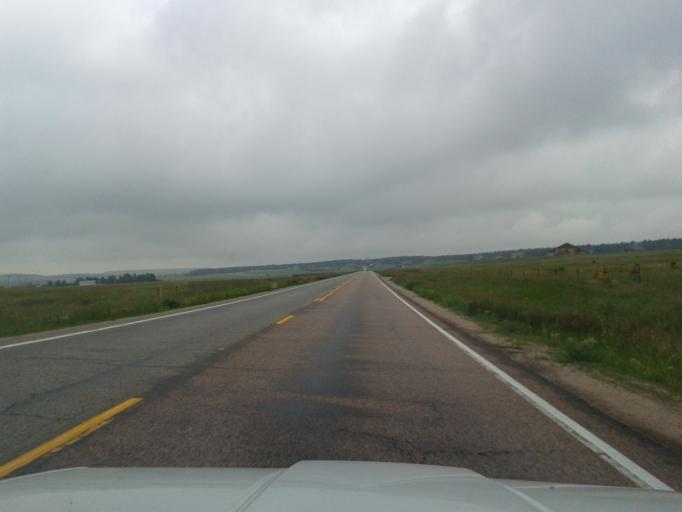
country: US
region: Colorado
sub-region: El Paso County
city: Woodmoor
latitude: 39.1143
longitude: -104.7705
